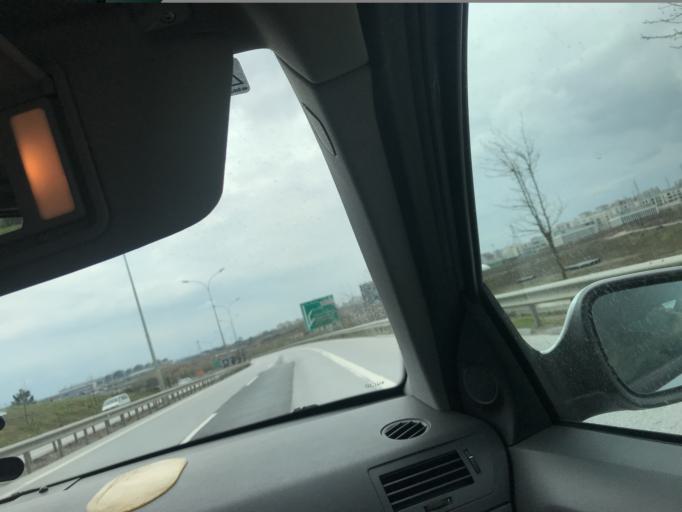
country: TR
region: Istanbul
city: Sultanbeyli
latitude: 40.9237
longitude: 29.3235
